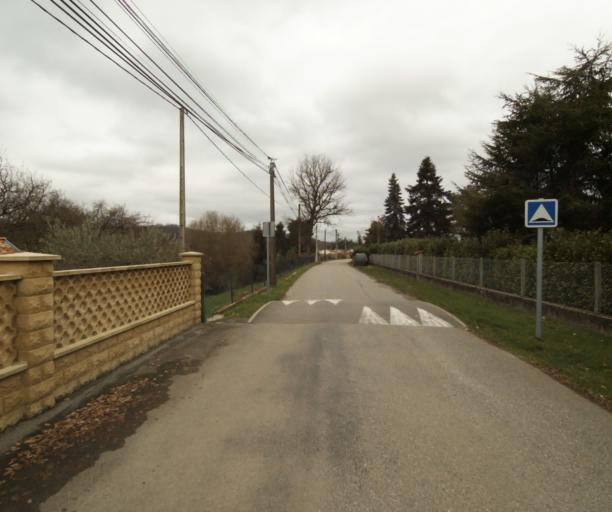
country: FR
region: Midi-Pyrenees
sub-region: Departement de l'Ariege
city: Pamiers
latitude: 43.1337
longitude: 1.6038
